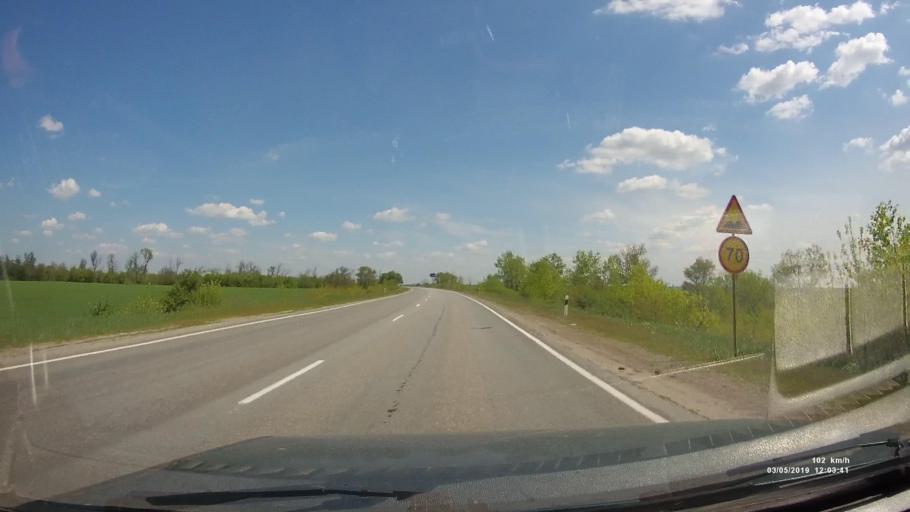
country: RU
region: Rostov
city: Bagayevskaya
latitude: 47.2743
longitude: 40.3958
